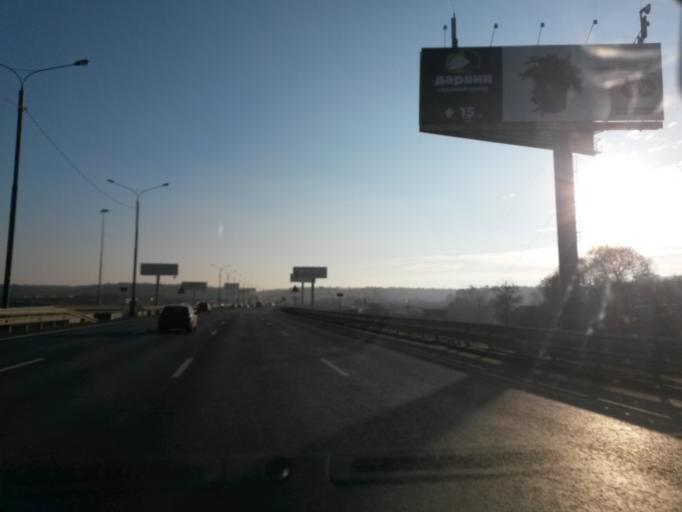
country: RU
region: Moscow
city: Annino
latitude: 55.5294
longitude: 37.6105
